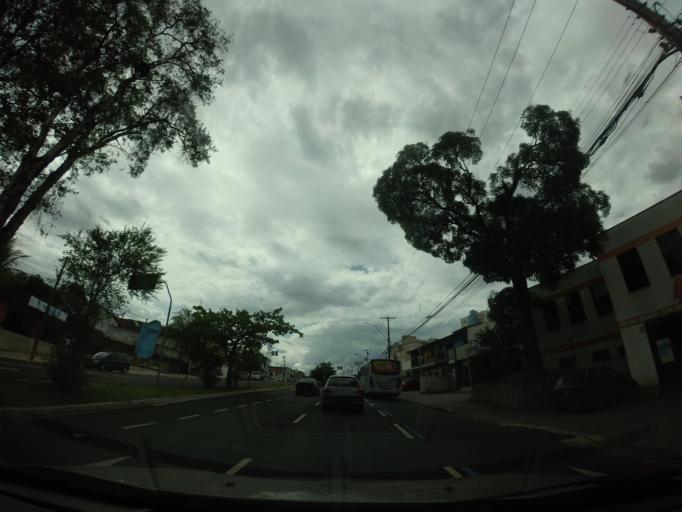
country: BR
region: Sao Paulo
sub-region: Piracicaba
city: Piracicaba
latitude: -22.7343
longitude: -47.6332
